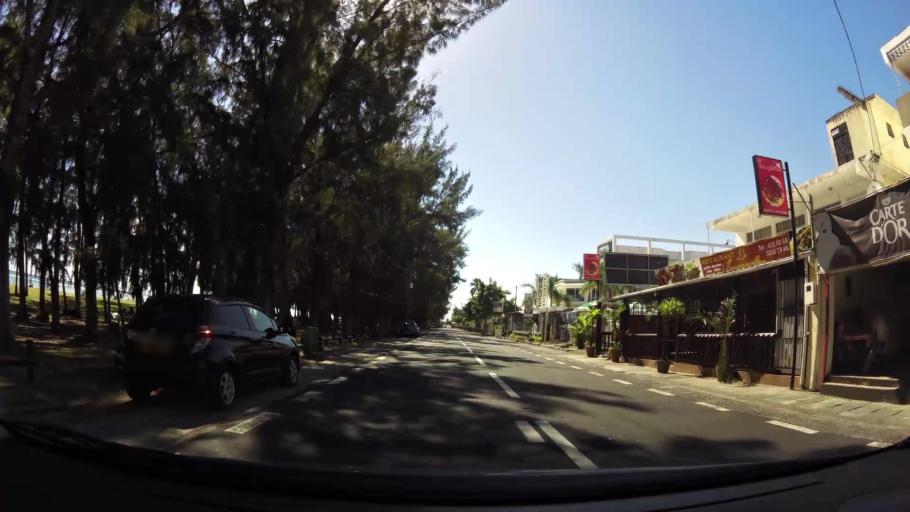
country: MU
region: Black River
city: Flic en Flac
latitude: -20.2834
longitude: 57.3649
